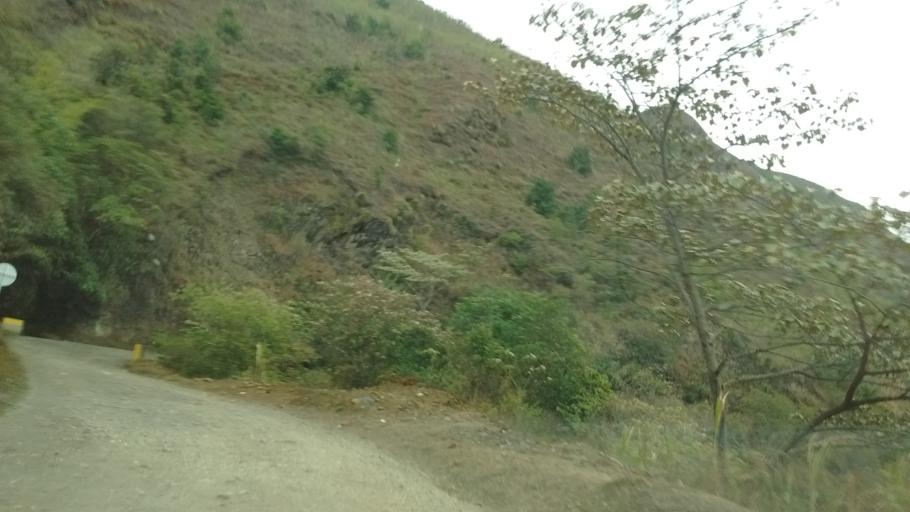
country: CO
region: Cauca
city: Almaguer
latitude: 1.8426
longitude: -76.9077
